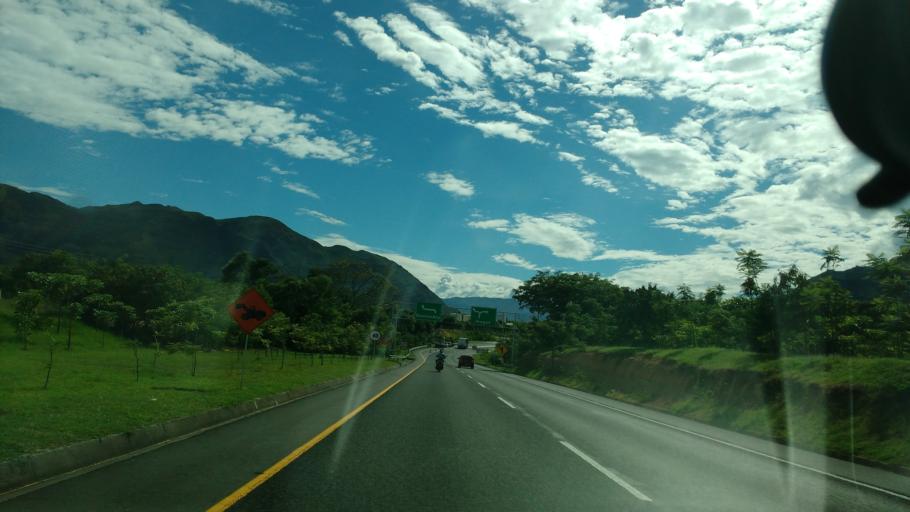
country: CO
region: Tolima
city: Valle de San Juan
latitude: 4.2778
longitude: -75.0103
